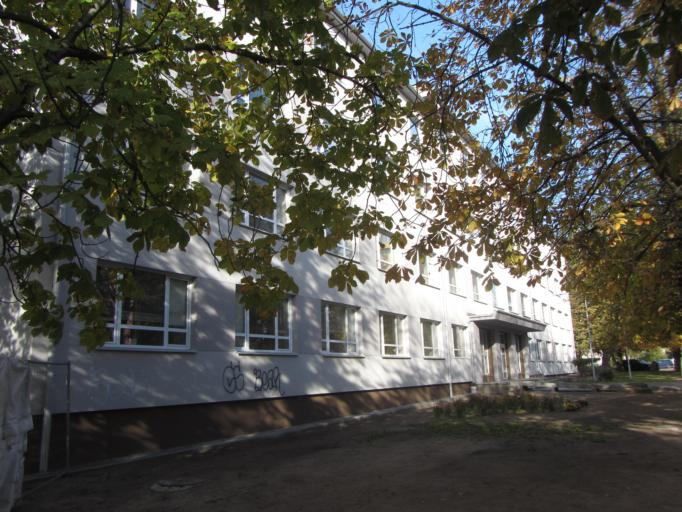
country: LT
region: Vilnius County
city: Vilkpede
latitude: 54.6787
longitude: 25.2538
